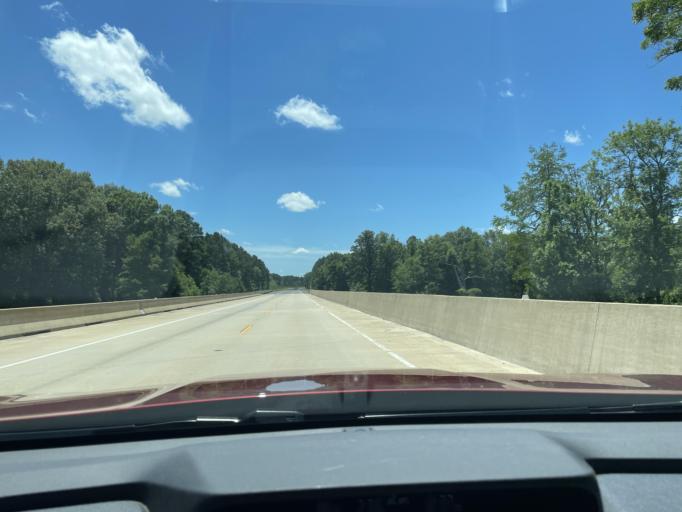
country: US
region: Arkansas
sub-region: Jefferson County
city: Pine Bluff
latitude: 34.1408
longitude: -91.9749
